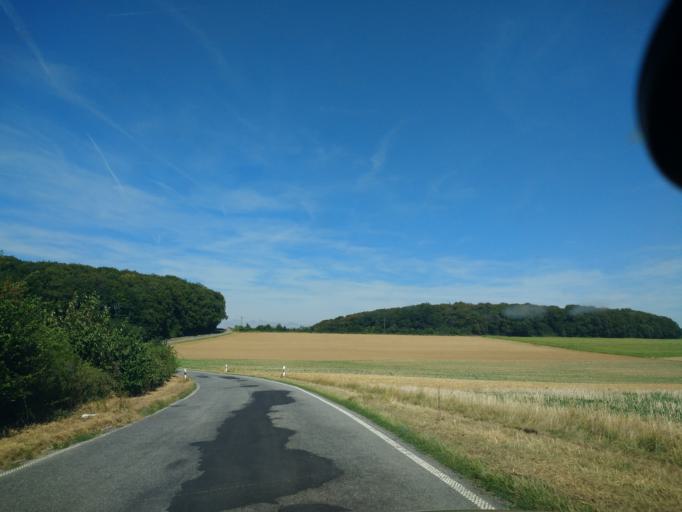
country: DE
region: Rheinland-Pfalz
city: Nittel
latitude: 49.6324
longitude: 6.4637
